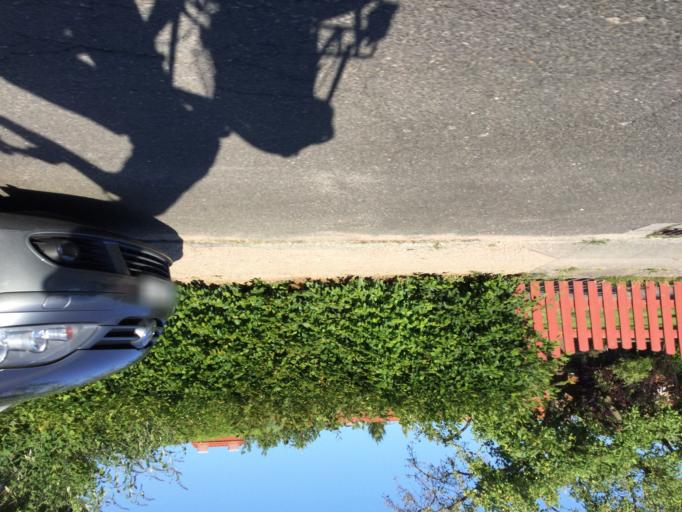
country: DE
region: Hamburg
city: Langenhorn
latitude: 53.6565
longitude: 10.0175
